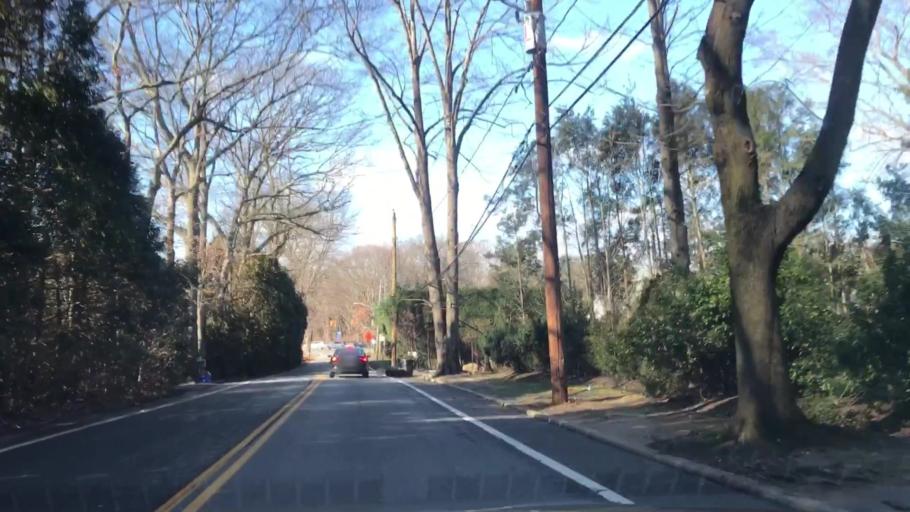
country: US
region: New York
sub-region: Suffolk County
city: Elwood
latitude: 40.8259
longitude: -73.3413
